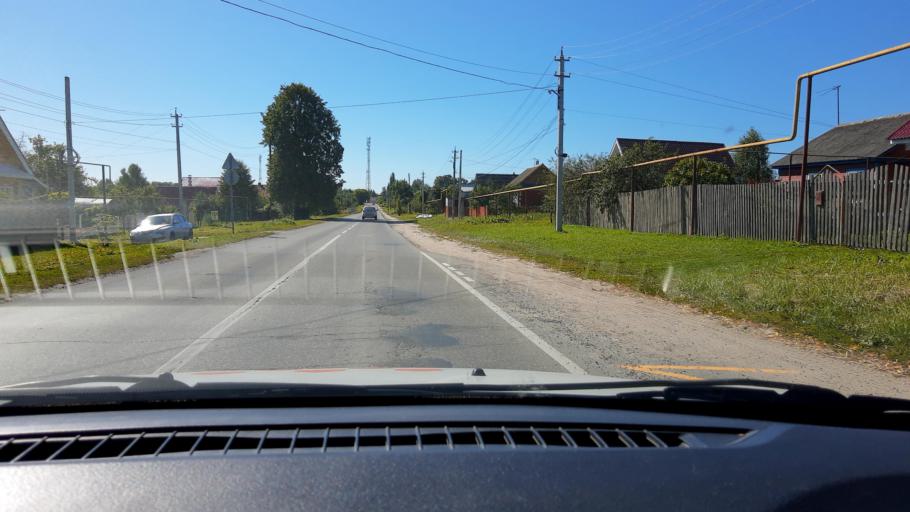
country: RU
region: Nizjnij Novgorod
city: Zavolzh'ye
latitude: 56.7222
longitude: 43.4139
